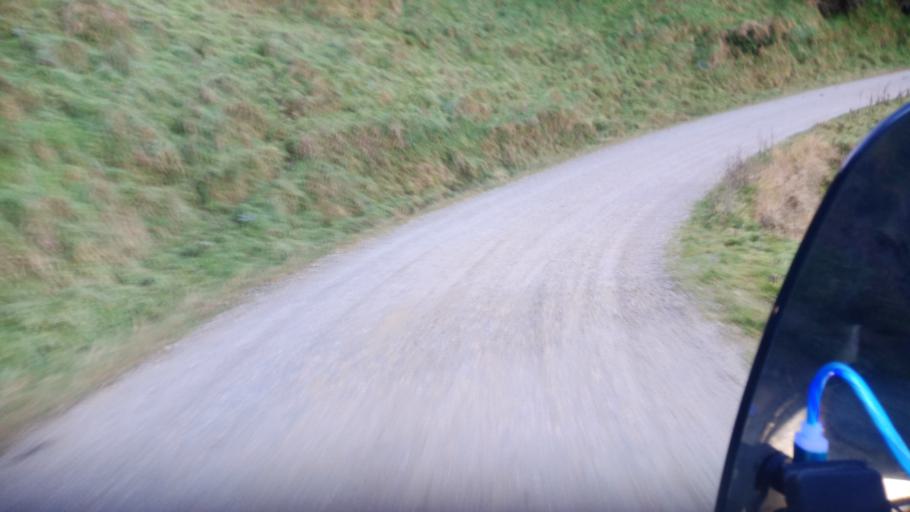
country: NZ
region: Hawke's Bay
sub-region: Wairoa District
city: Wairoa
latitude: -38.6651
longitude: 177.4797
